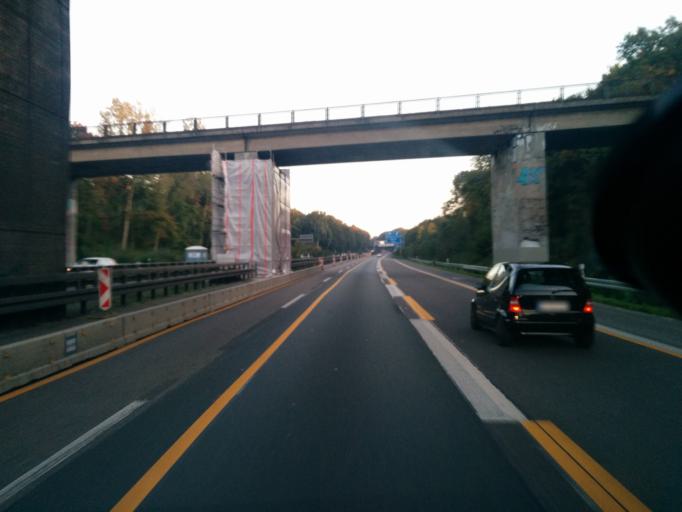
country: DE
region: North Rhine-Westphalia
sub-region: Regierungsbezirk Arnsberg
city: Bochum
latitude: 51.4812
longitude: 7.2790
